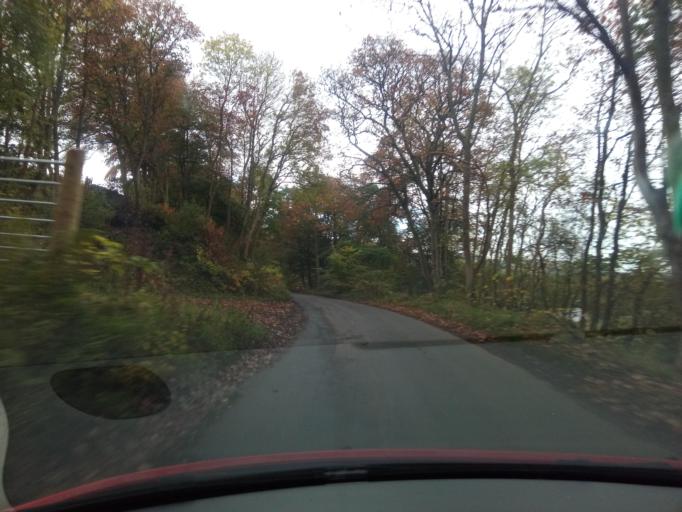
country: GB
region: Scotland
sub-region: The Scottish Borders
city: Innerleithen
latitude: 55.6389
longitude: -3.1163
